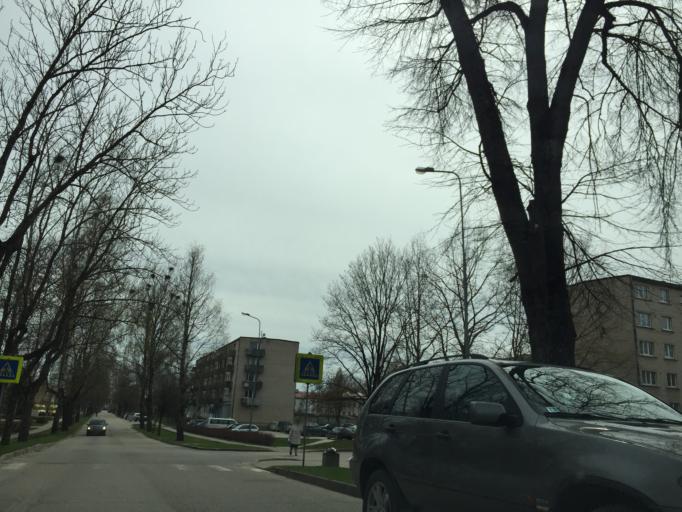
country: LV
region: Ludzas Rajons
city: Ludza
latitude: 56.5421
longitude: 27.7207
